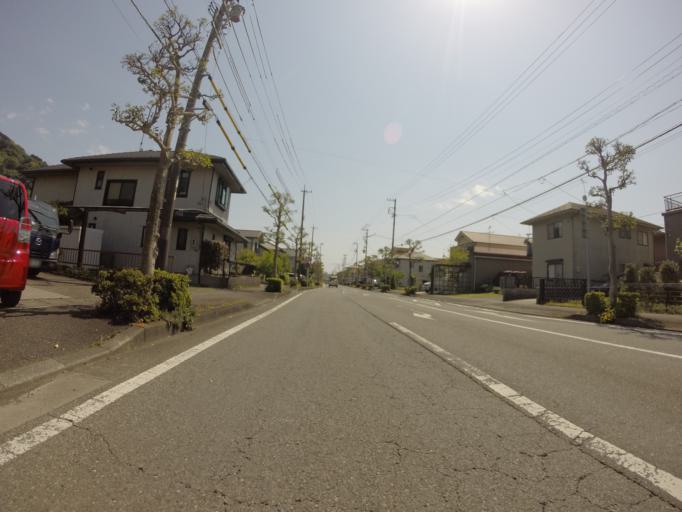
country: JP
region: Shizuoka
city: Shizuoka-shi
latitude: 35.0341
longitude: 138.4268
